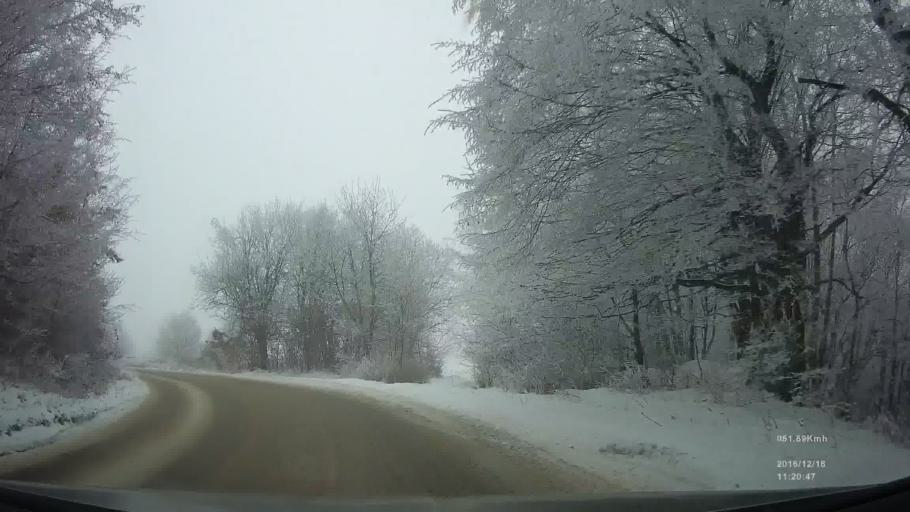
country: SK
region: Presovsky
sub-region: Okres Presov
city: Presov
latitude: 48.9078
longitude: 21.3625
